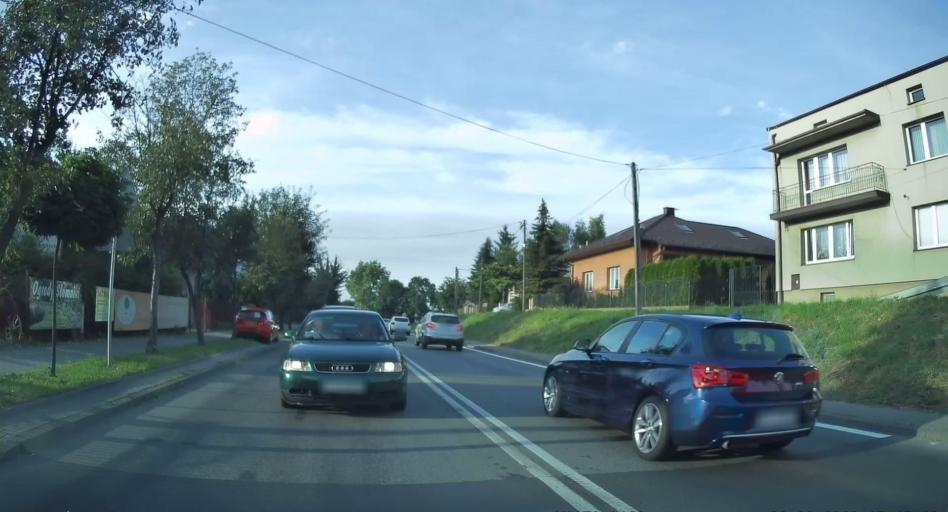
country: PL
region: Lesser Poland Voivodeship
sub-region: Powiat krakowski
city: Slomniki
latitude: 50.2463
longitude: 20.0840
